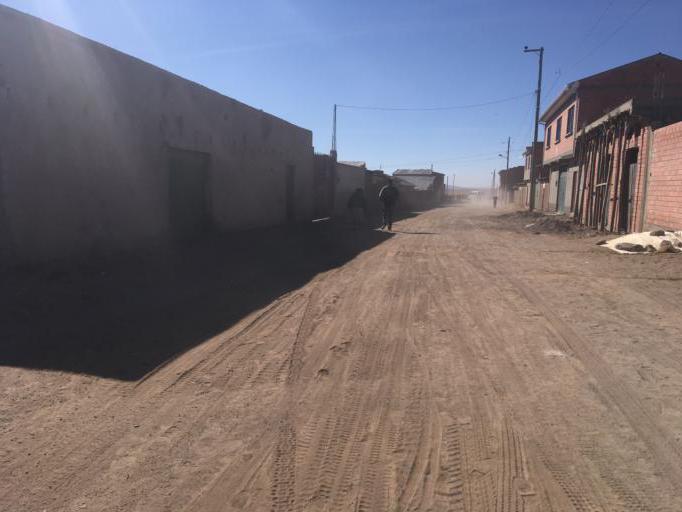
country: PE
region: Puno
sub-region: Provincia de Chucuito
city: Kelluyo
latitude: -17.0664
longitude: -69.1907
